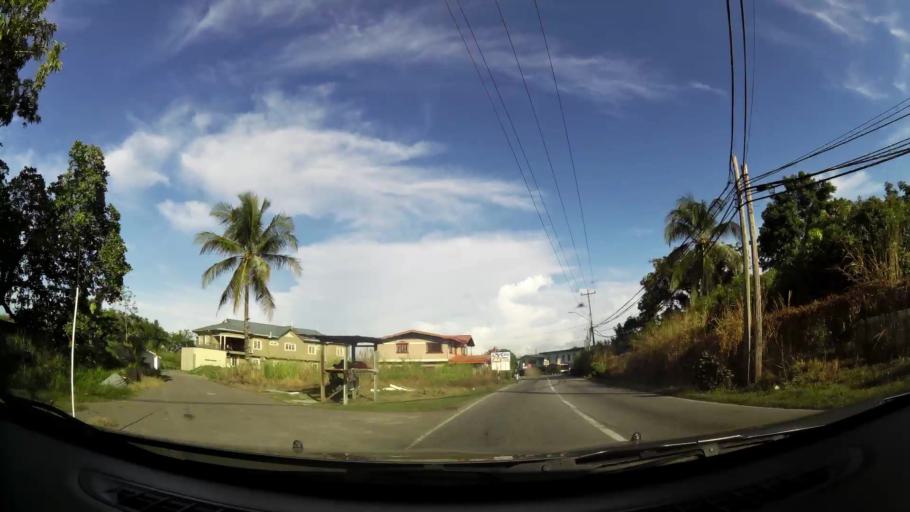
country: TT
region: Chaguanas
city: Chaguanas
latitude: 10.5469
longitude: -61.3540
